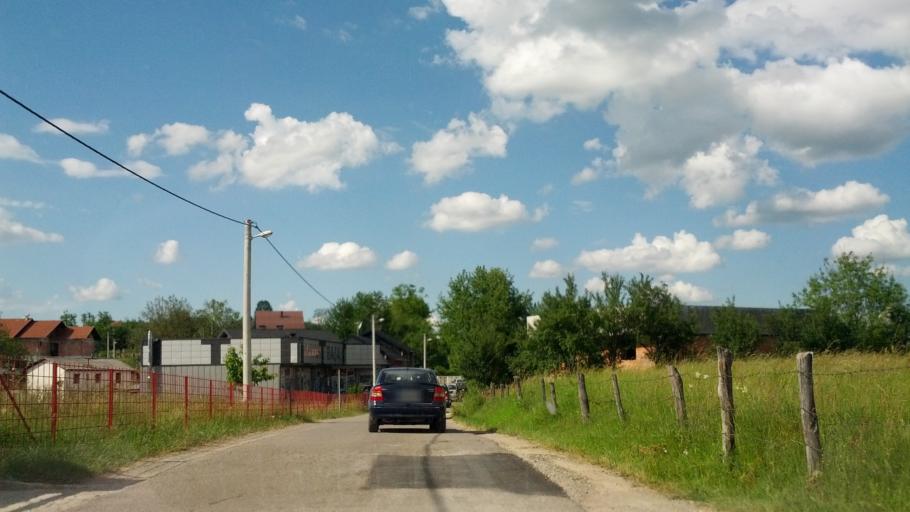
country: BA
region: Federation of Bosnia and Herzegovina
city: Ostrozac
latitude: 44.9226
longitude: 15.9564
